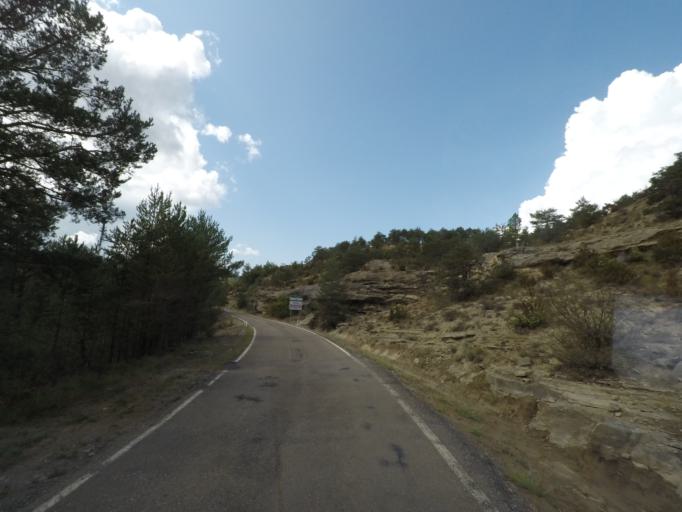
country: ES
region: Aragon
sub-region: Provincia de Huesca
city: Yebra de Basa
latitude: 42.3902
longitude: -0.3092
